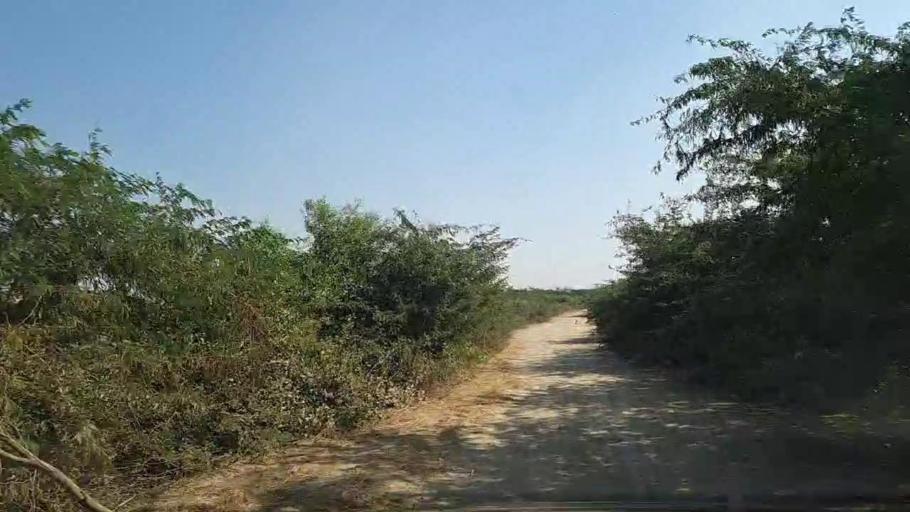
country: PK
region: Sindh
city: Daro Mehar
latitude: 24.8104
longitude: 68.0747
